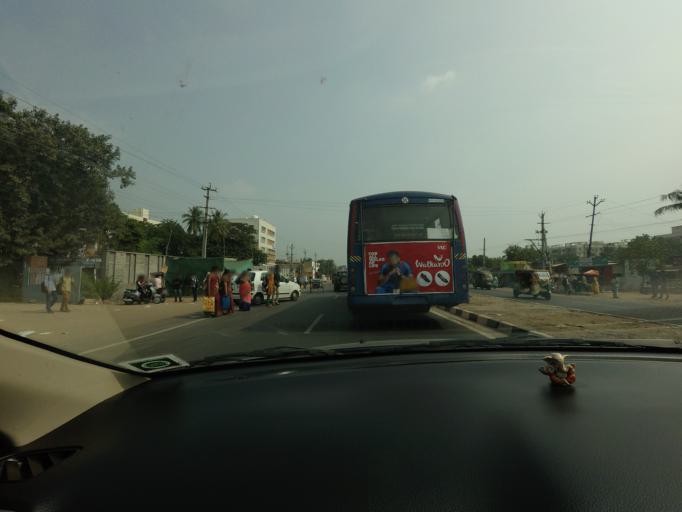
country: IN
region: Andhra Pradesh
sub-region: Krishna
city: Yanamalakuduru
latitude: 16.4821
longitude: 80.6911
